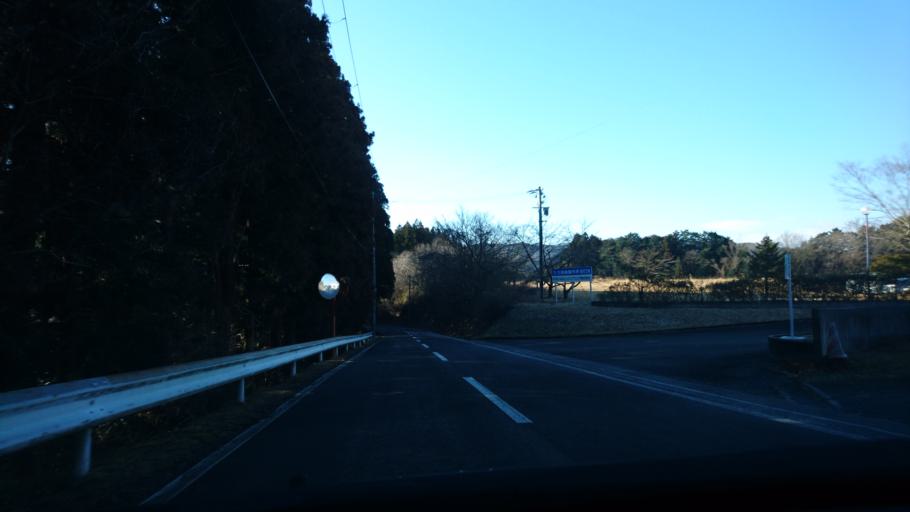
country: JP
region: Iwate
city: Ichinoseki
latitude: 38.8552
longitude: 141.2977
